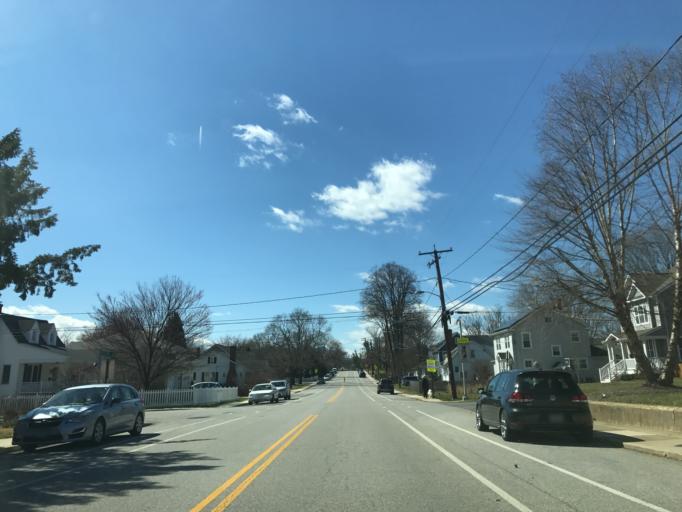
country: US
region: Maryland
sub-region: Anne Arundel County
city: Naval Academy
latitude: 38.9926
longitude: -76.5012
